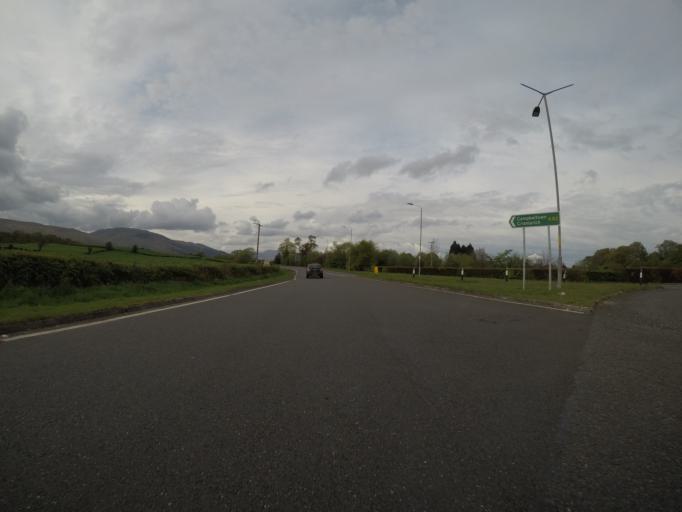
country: GB
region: Scotland
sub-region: West Dunbartonshire
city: Balloch
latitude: 56.0267
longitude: -4.6343
